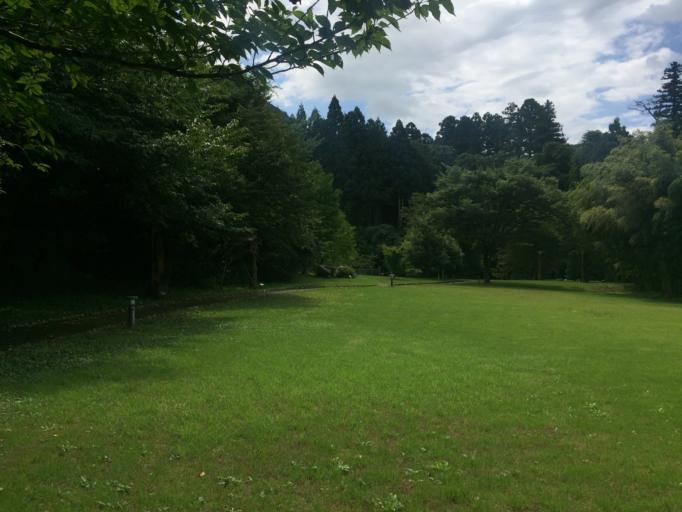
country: JP
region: Toyama
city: Nanto-shi
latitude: 36.5612
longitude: 136.9755
